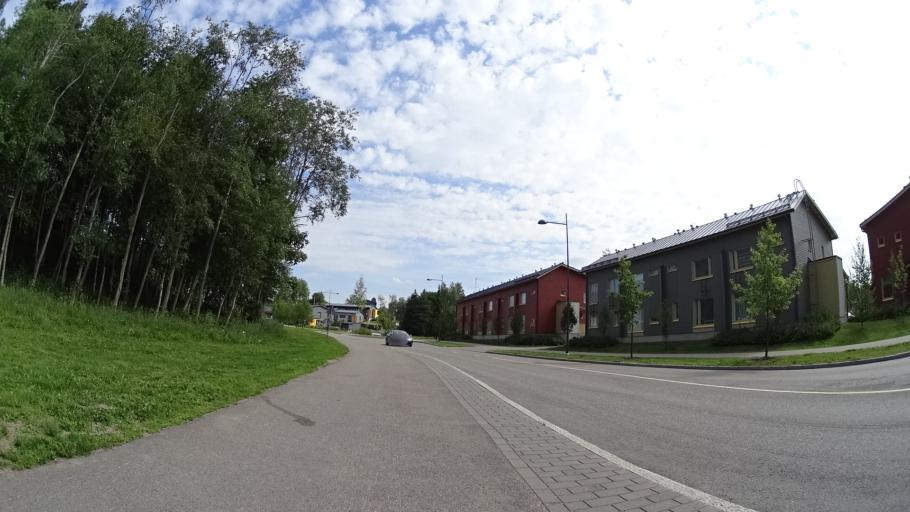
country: FI
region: Uusimaa
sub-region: Helsinki
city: Espoo
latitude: 60.1923
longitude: 24.5921
